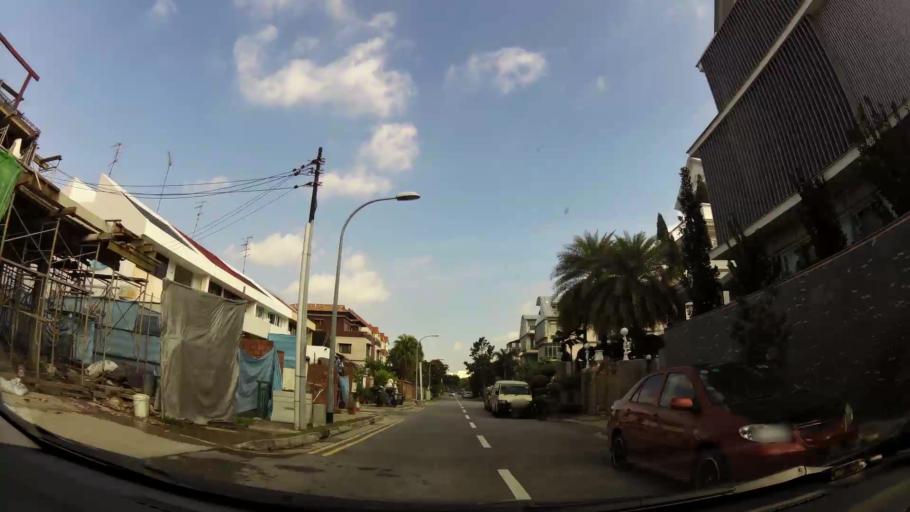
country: SG
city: Singapore
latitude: 1.3226
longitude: 103.9088
